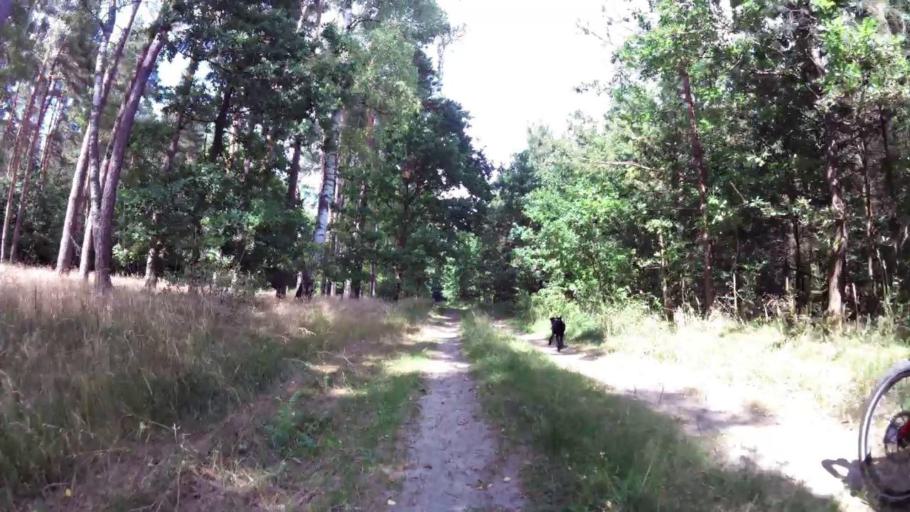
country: PL
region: West Pomeranian Voivodeship
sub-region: Powiat lobeski
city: Lobez
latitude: 53.6116
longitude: 15.6716
